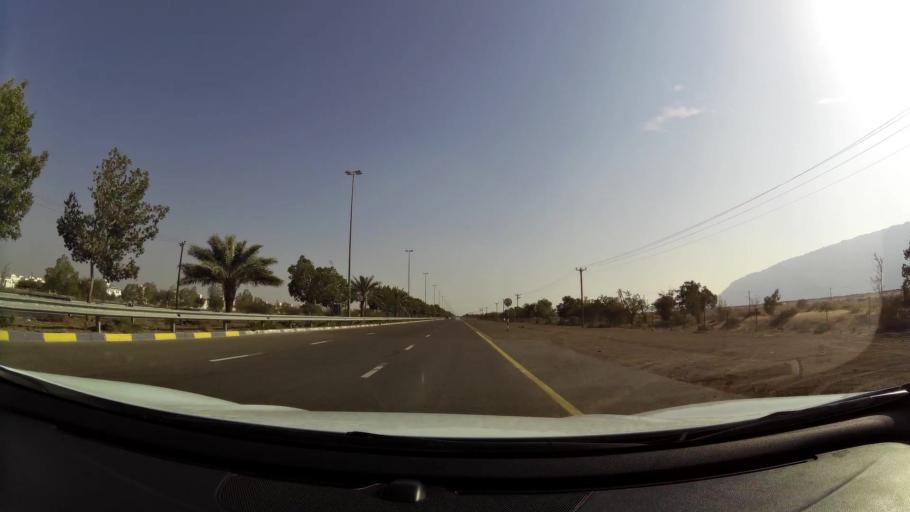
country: AE
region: Abu Dhabi
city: Al Ain
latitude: 24.0634
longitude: 55.8375
